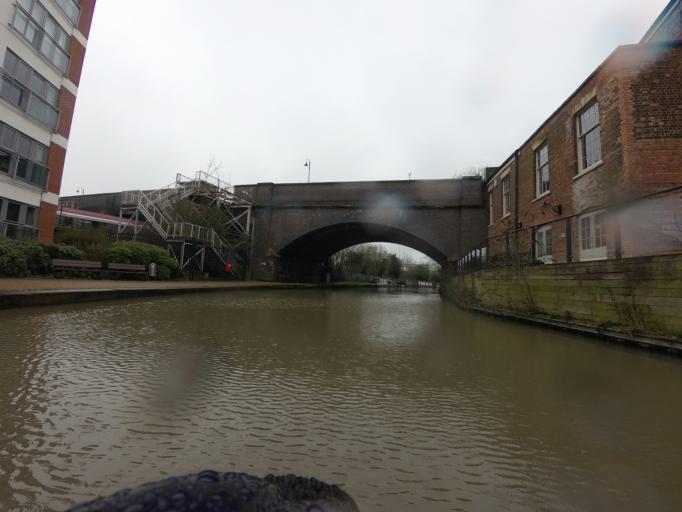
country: GB
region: England
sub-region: Milton Keynes
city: Bradwell
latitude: 52.0648
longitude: -0.8046
